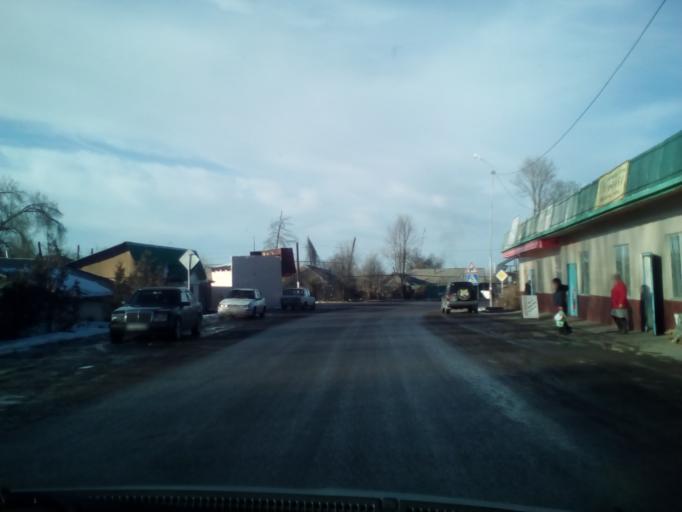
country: KZ
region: Almaty Oblysy
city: Burunday
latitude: 43.1617
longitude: 76.4163
